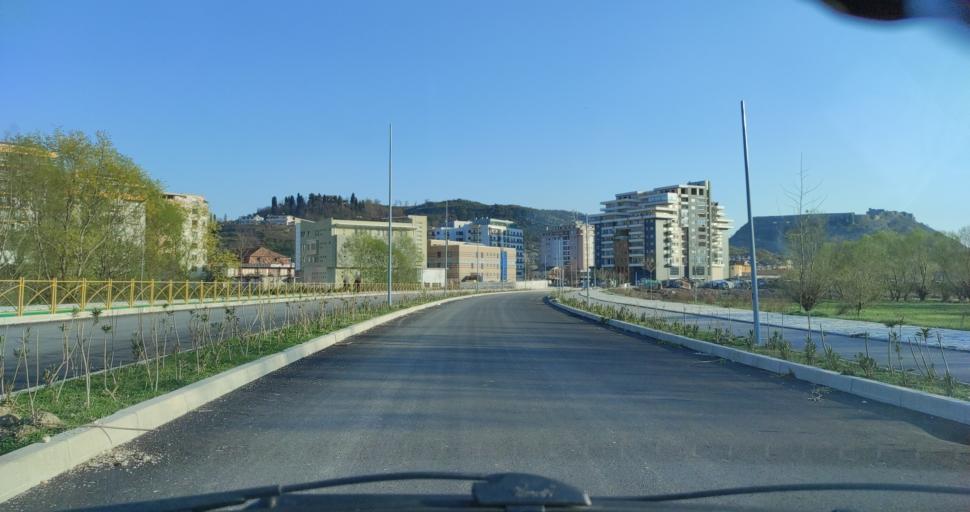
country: AL
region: Shkoder
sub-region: Rrethi i Shkodres
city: Shkoder
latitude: 42.0579
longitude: 19.4983
